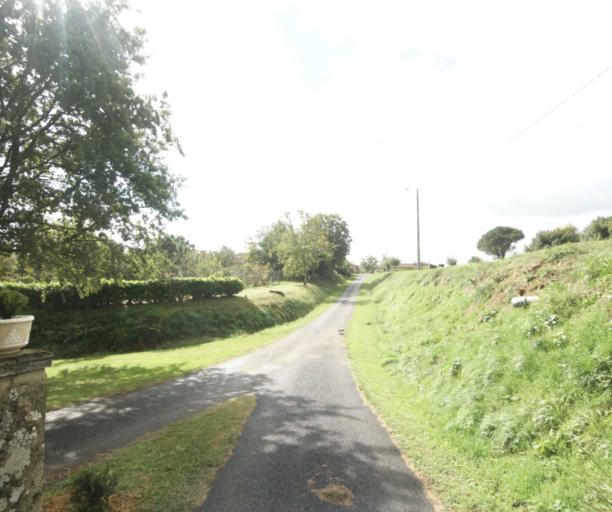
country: FR
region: Midi-Pyrenees
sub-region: Departement du Gers
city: Nogaro
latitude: 43.8204
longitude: -0.0853
